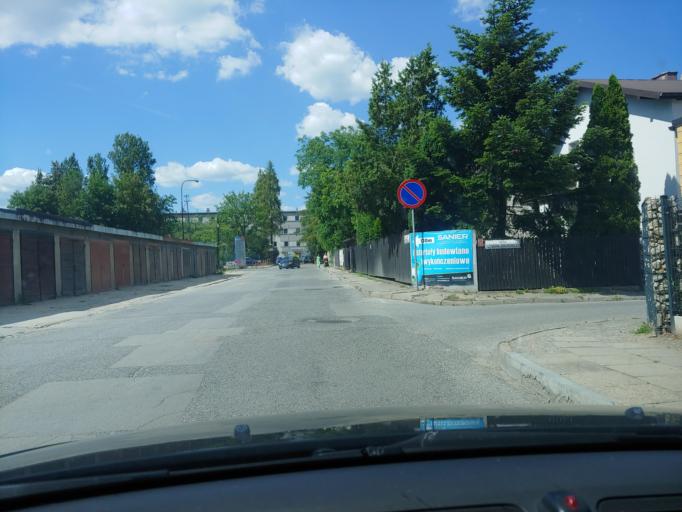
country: PL
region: Lesser Poland Voivodeship
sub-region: Powiat krakowski
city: Zielonki
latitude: 50.0946
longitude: 19.9247
